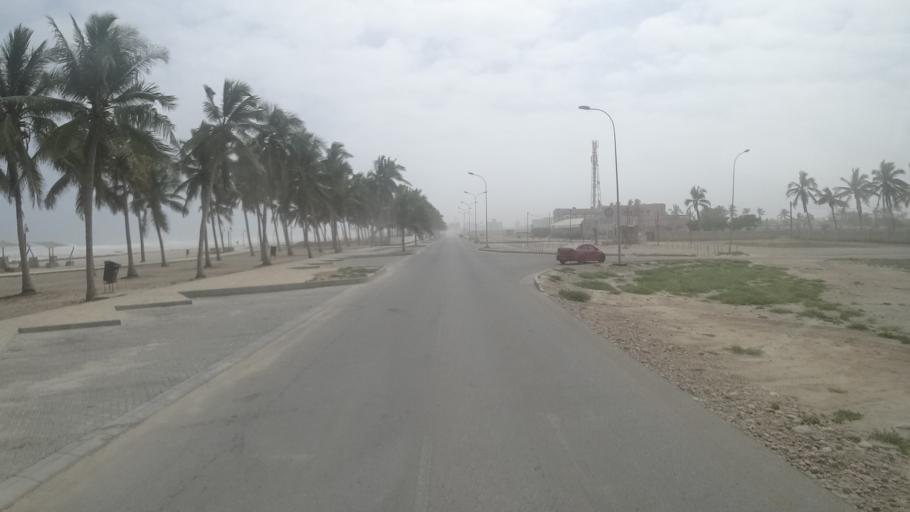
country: OM
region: Zufar
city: Salalah
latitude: 17.0113
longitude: 54.1733
